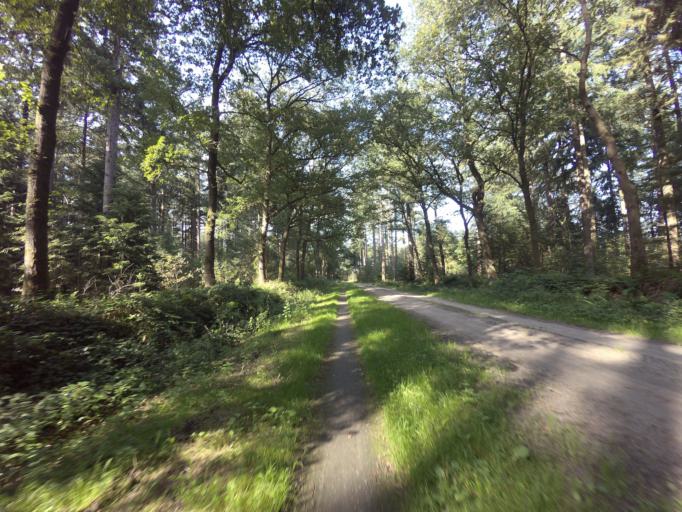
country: NL
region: Drenthe
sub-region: Gemeente Tynaarlo
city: Vries
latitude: 53.0668
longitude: 6.5069
